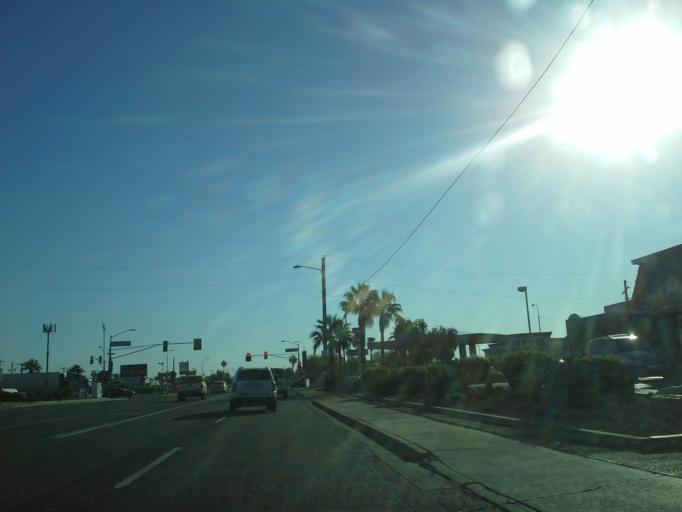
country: US
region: Arizona
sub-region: Maricopa County
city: Glendale
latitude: 33.4804
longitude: -112.1529
